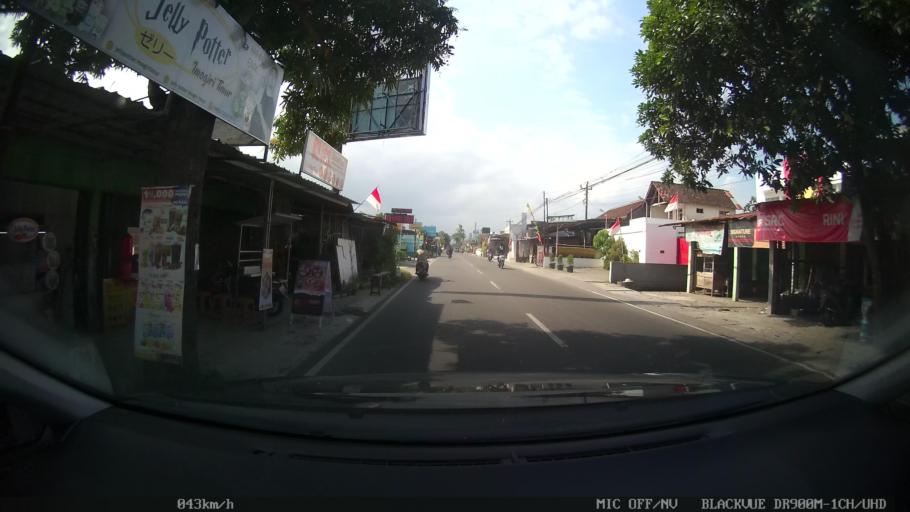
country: ID
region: Daerah Istimewa Yogyakarta
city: Sewon
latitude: -7.8601
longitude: 110.3895
